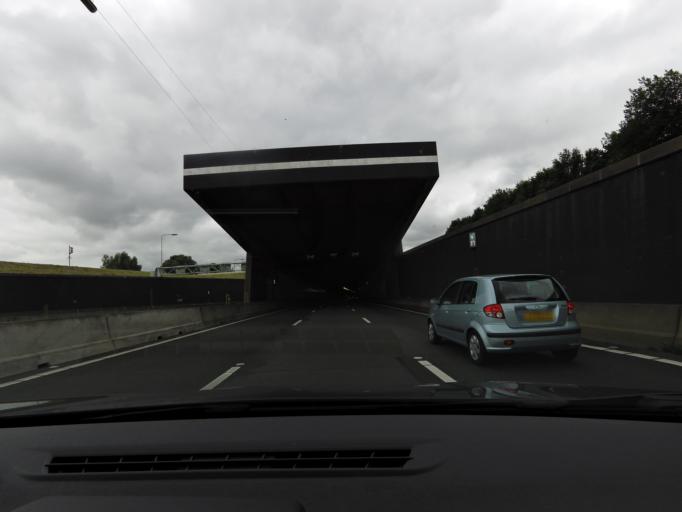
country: NL
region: South Holland
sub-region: Gemeente Barendrecht
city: Barendrecht
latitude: 51.8367
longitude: 4.5139
